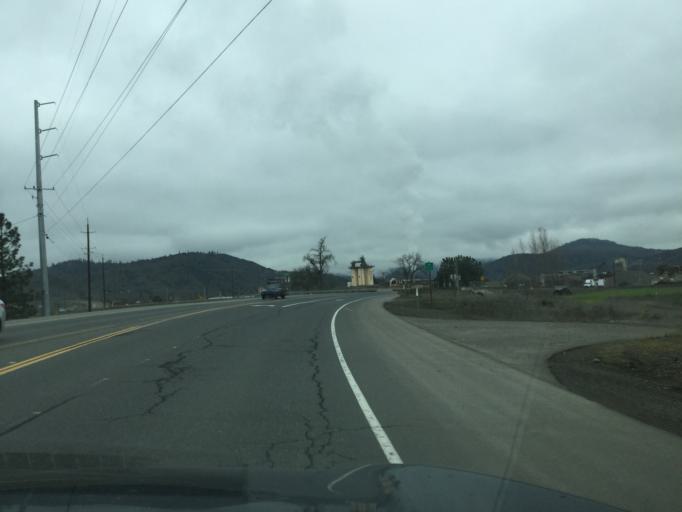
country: US
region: Oregon
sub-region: Jackson County
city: Central Point
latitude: 42.4200
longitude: -122.9562
